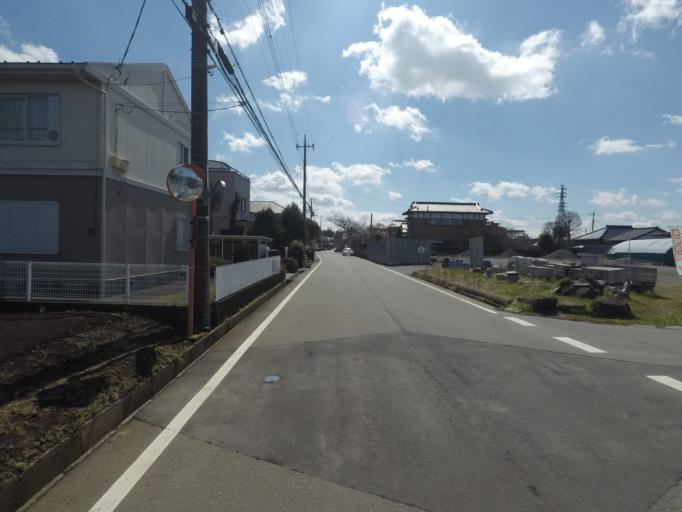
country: JP
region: Ibaraki
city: Naka
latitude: 36.0487
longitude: 140.1107
